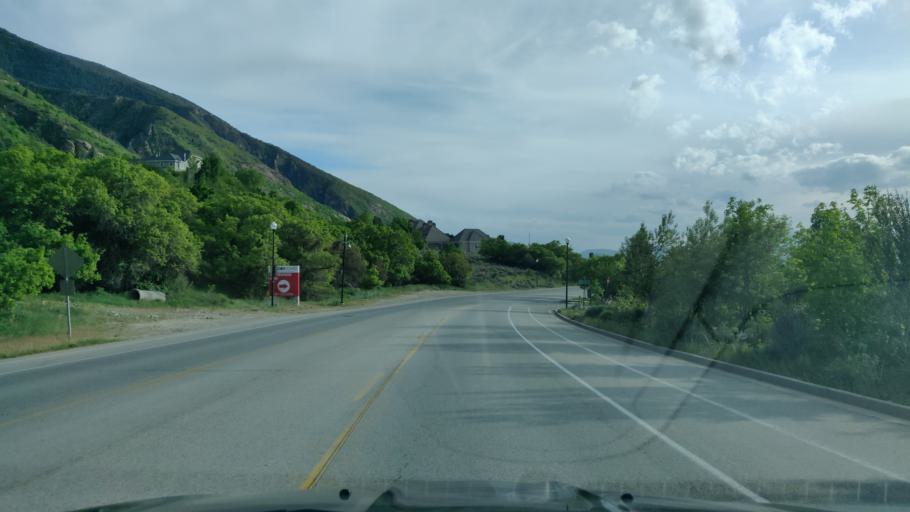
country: US
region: Utah
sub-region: Salt Lake County
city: Granite
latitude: 40.5514
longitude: -111.8030
